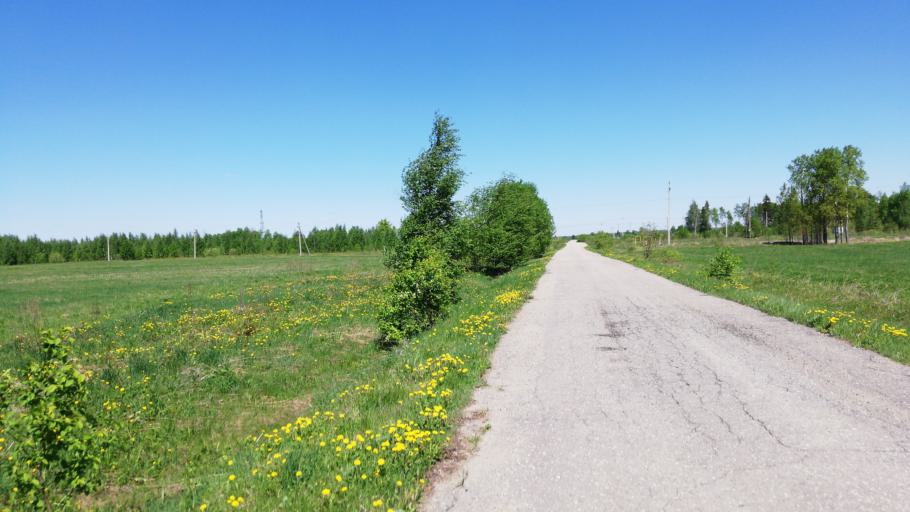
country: RU
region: Ivanovo
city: Pistsovo
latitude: 57.1226
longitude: 40.5996
